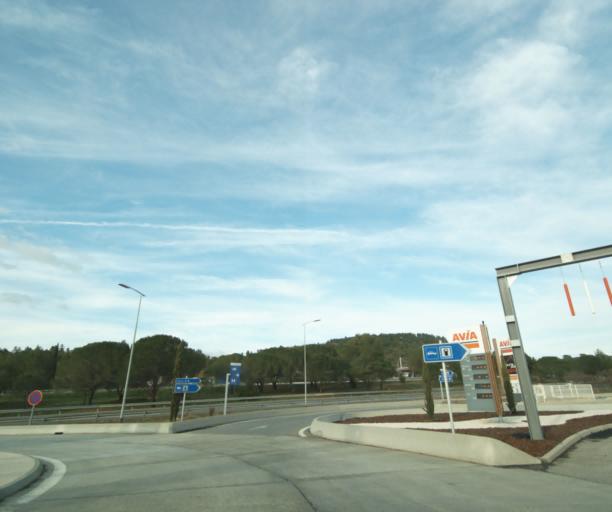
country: FR
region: Provence-Alpes-Cote d'Azur
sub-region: Departement du Var
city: Vidauban
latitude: 43.4142
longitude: 6.4520
